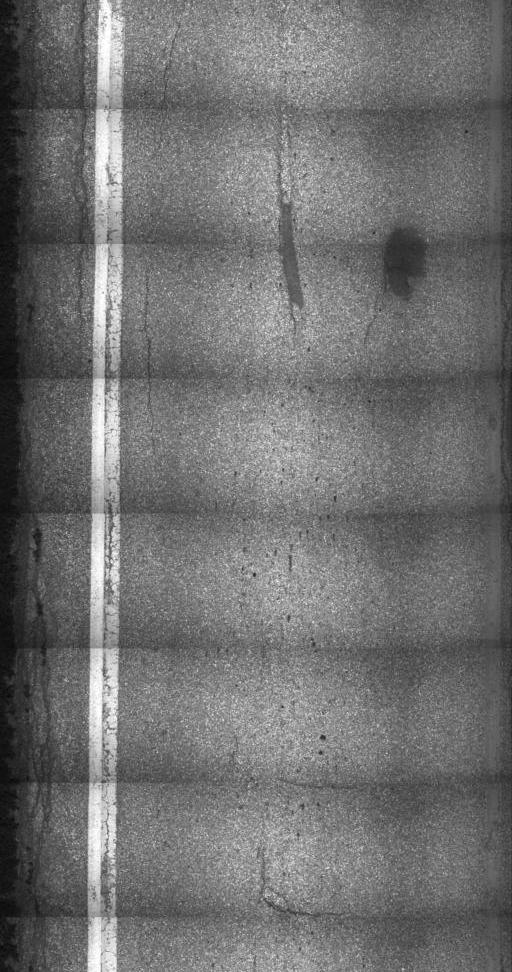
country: US
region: Vermont
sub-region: Franklin County
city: Enosburg Falls
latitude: 44.9478
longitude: -72.9048
